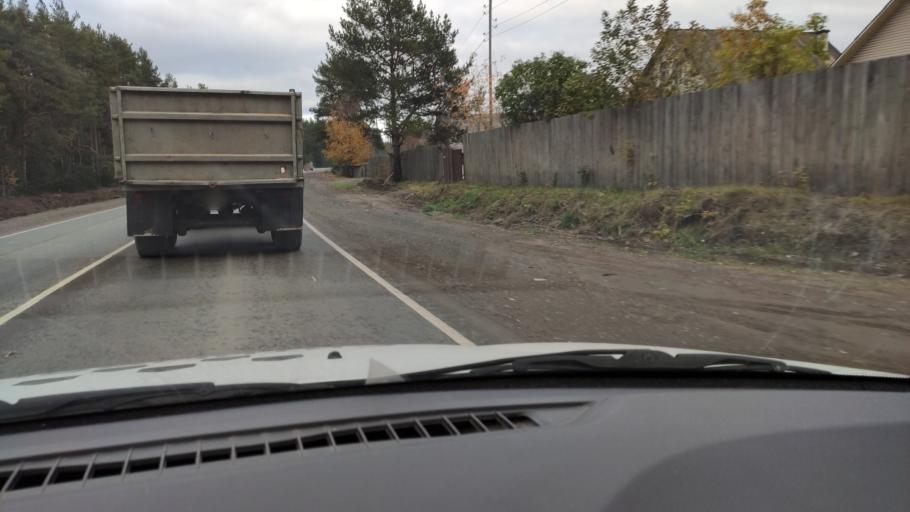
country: RU
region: Kirov
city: Belaya Kholunitsa
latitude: 58.8515
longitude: 50.8302
